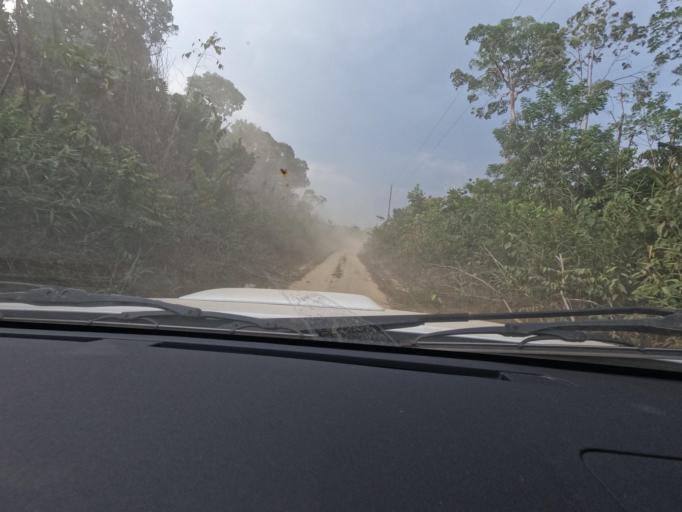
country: BR
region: Rondonia
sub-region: Porto Velho
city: Porto Velho
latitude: -8.5672
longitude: -64.0225
